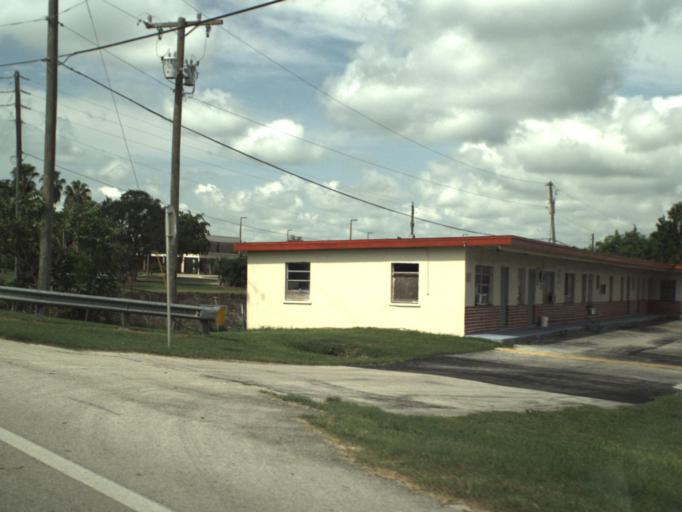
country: US
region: Florida
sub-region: Palm Beach County
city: Belle Glade
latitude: 26.6786
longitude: -80.6863
